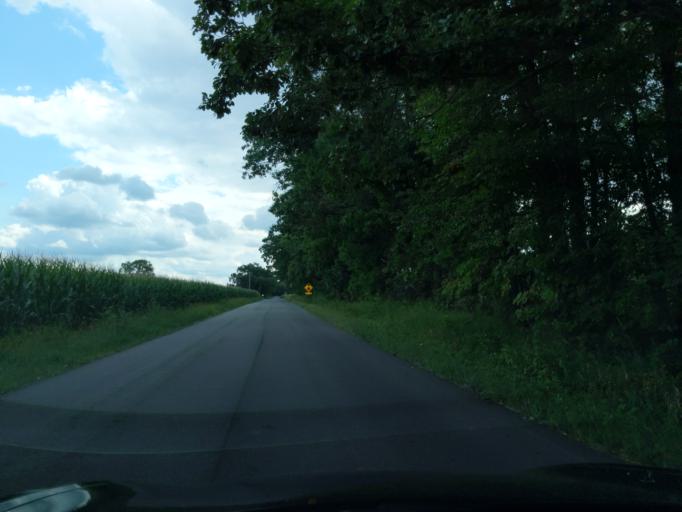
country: US
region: Michigan
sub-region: Eaton County
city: Eaton Rapids
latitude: 42.4533
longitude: -84.5804
